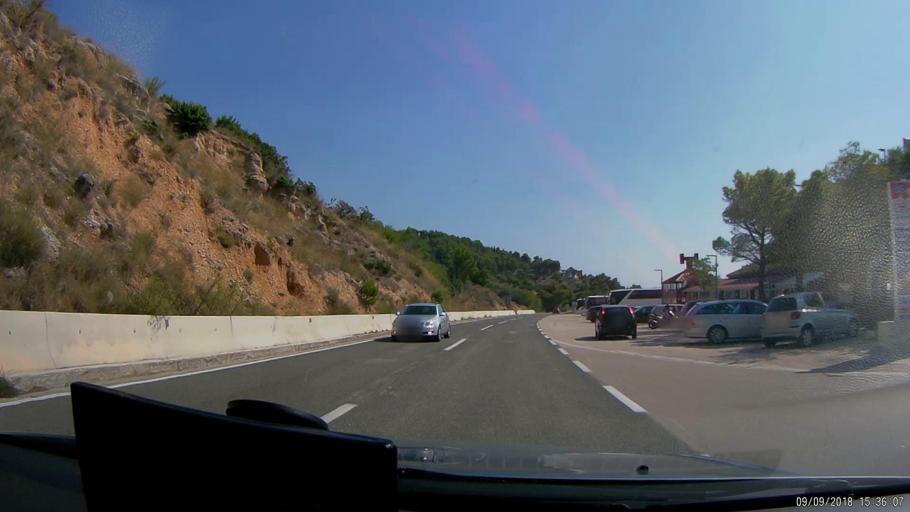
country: HR
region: Splitsko-Dalmatinska
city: Donja Brela
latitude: 43.3808
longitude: 16.9213
